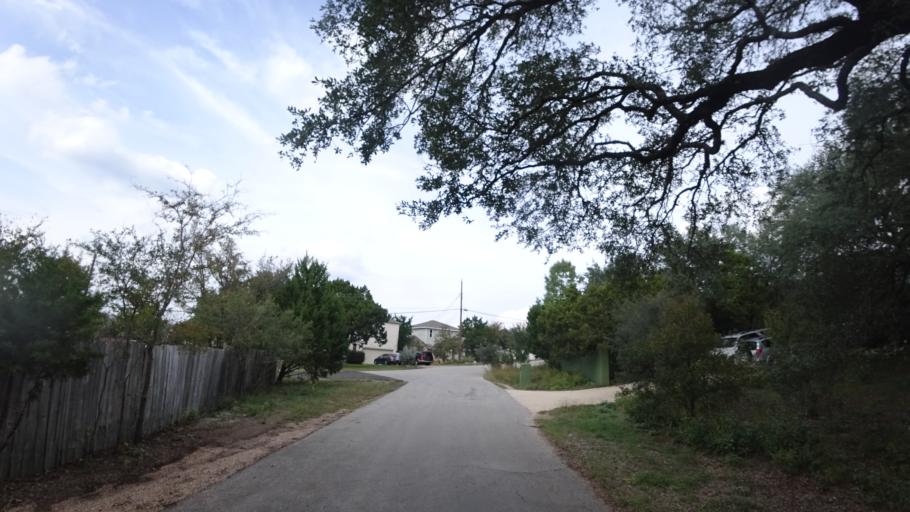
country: US
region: Texas
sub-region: Travis County
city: Hudson Bend
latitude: 30.3824
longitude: -97.9188
